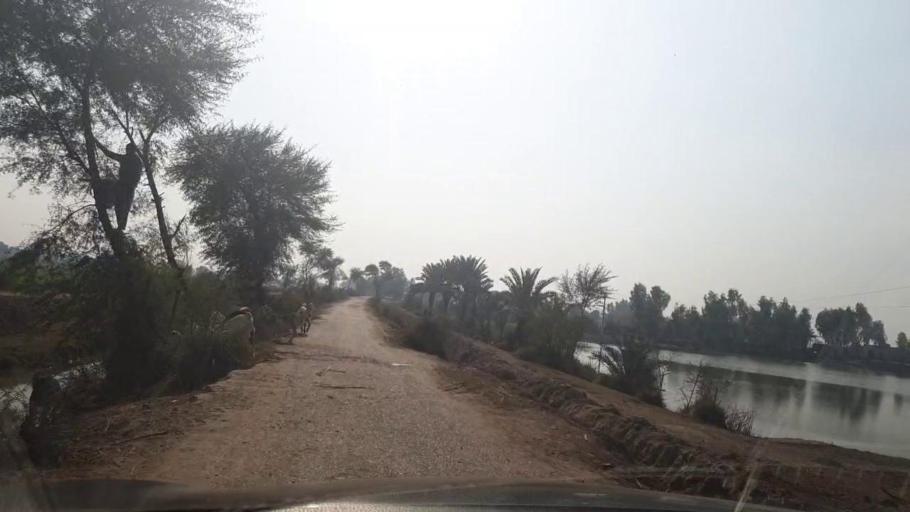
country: PK
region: Sindh
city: Khairpur
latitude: 28.1137
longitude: 69.6395
